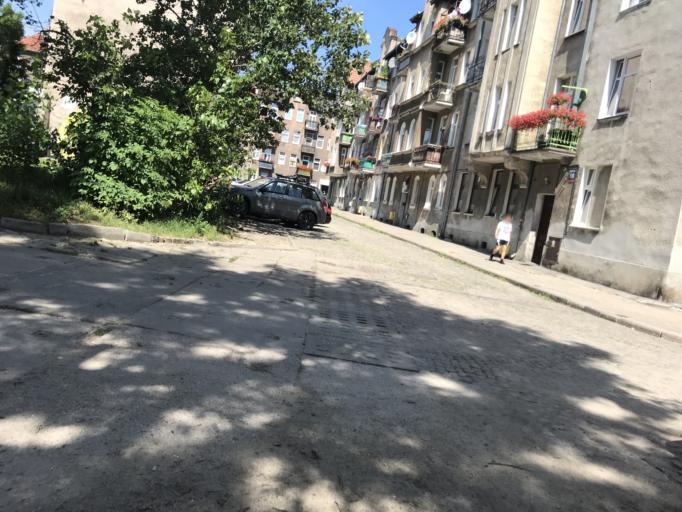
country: PL
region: Pomeranian Voivodeship
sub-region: Gdansk
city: Gdansk
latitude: 54.3419
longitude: 18.6646
